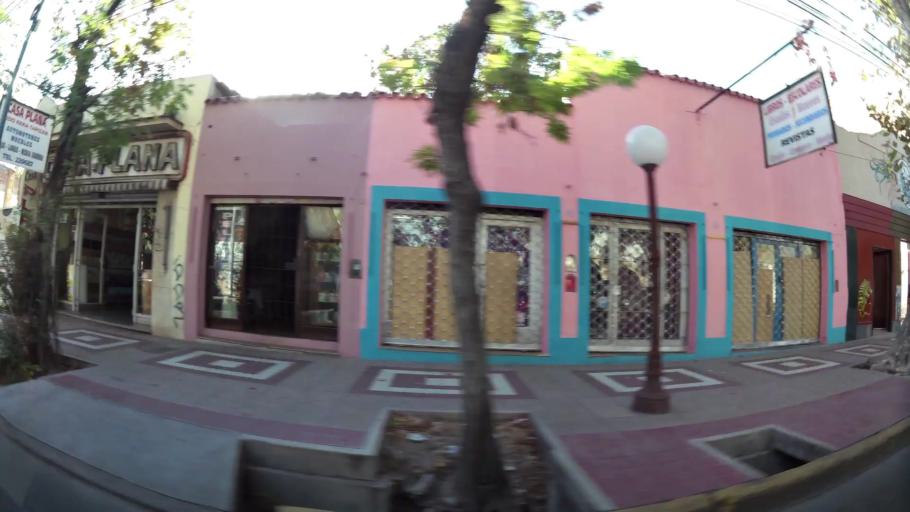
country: AR
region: Mendoza
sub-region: Departamento de Godoy Cruz
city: Godoy Cruz
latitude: -32.9278
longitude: -68.8444
